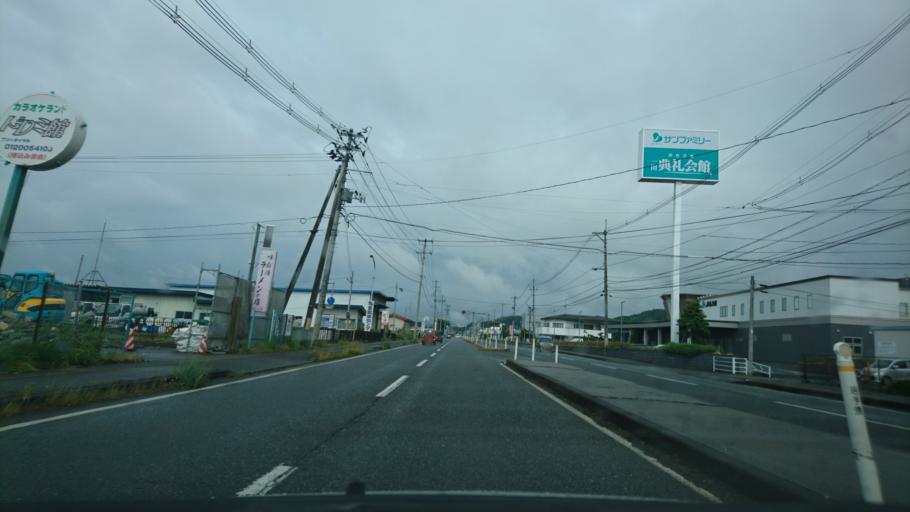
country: JP
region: Iwate
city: Ichinoseki
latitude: 38.9394
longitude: 141.0985
